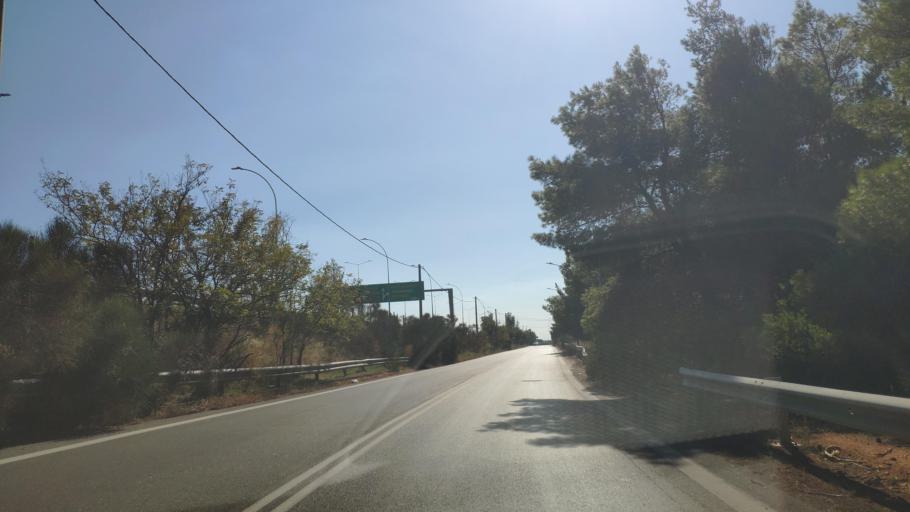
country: GR
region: Attica
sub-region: Nomarchia Athinas
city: Ekali
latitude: 38.1122
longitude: 23.8235
